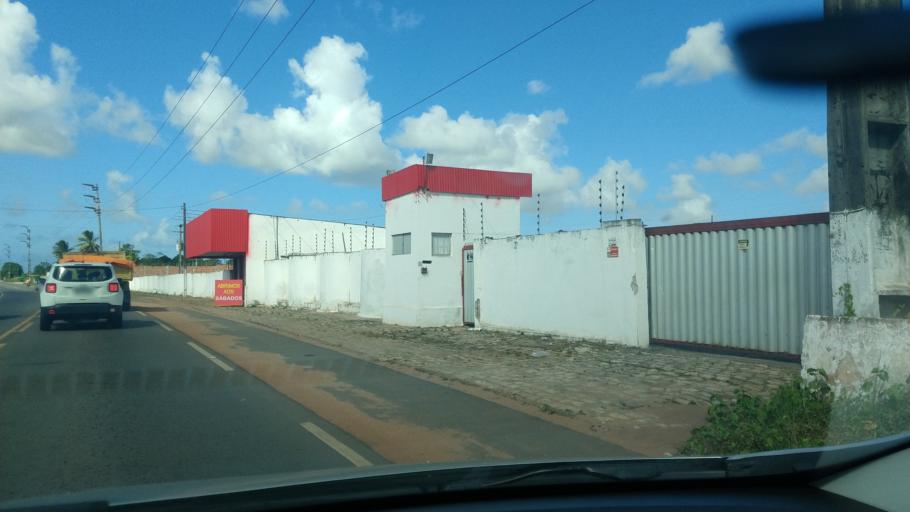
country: BR
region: Rio Grande do Norte
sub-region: Sao Goncalo Do Amarante
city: Sao Goncalo do Amarante
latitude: -5.7884
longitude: -35.2976
